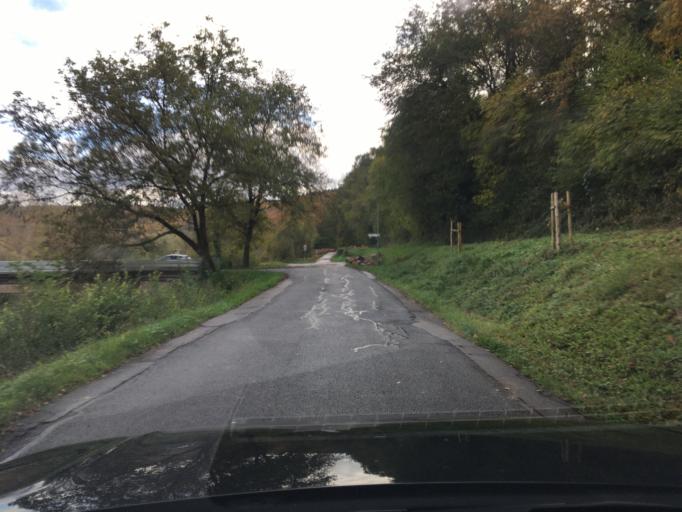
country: DE
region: Baden-Wuerttemberg
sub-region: Regierungsbezirk Stuttgart
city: Mockmuhl
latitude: 49.3192
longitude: 9.3751
